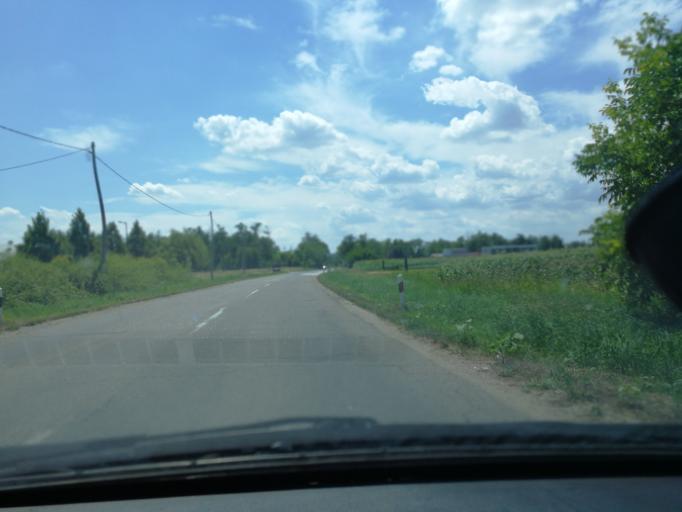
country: HU
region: Pest
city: Kiskunlachaza
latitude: 47.1628
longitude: 18.9998
